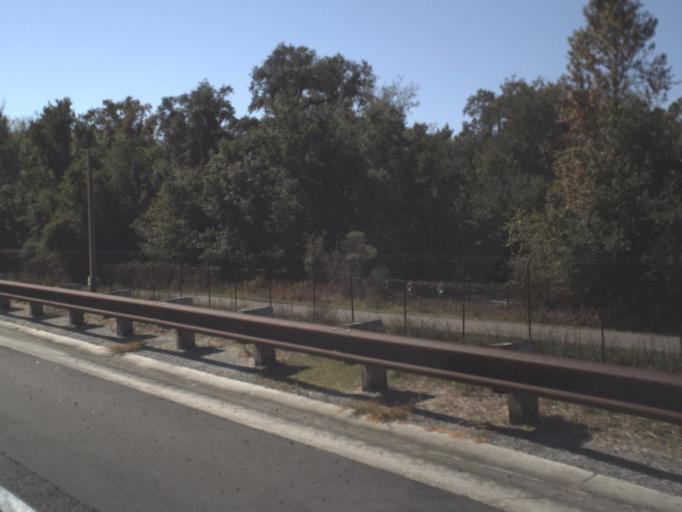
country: US
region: Florida
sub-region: Hernando County
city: Brookridge
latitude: 28.6378
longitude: -82.4896
